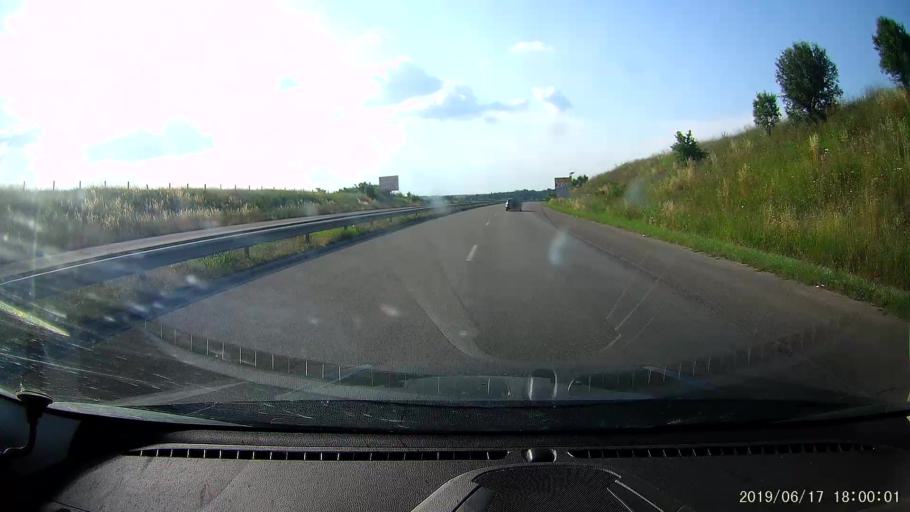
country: BG
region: Khaskovo
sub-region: Obshtina Svilengrad
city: Svilengrad
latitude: 41.7300
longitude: 26.2852
